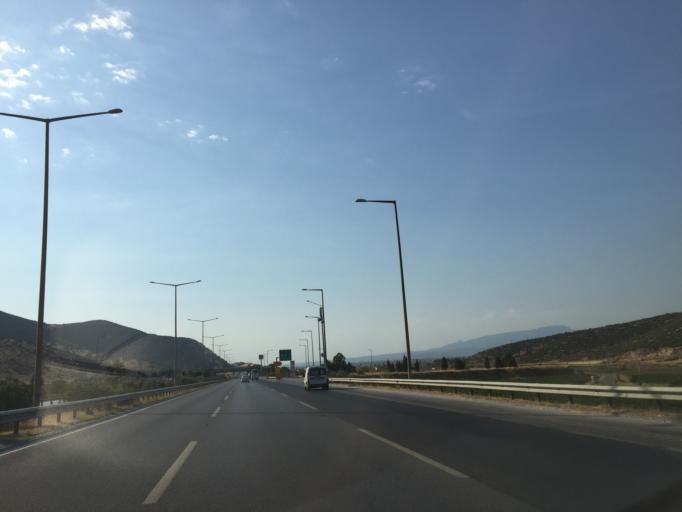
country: TR
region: Izmir
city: Belevi
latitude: 38.0655
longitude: 27.4160
